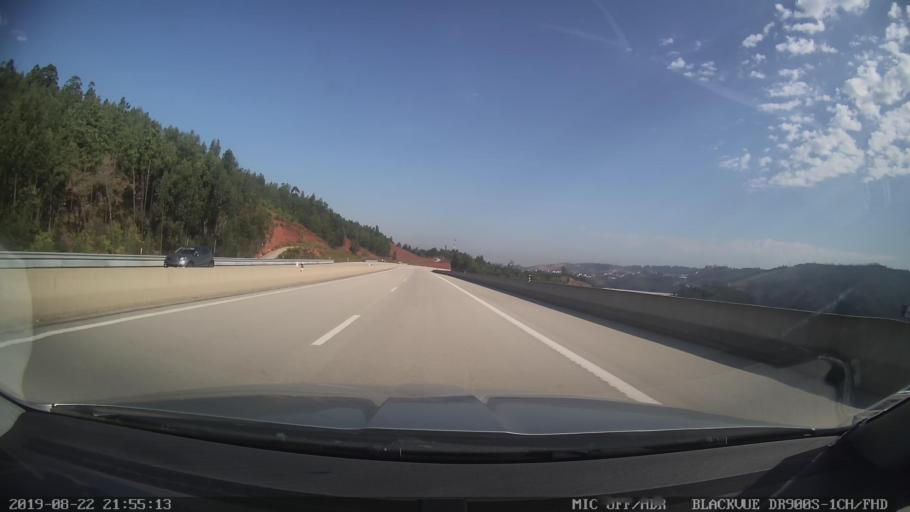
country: PT
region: Coimbra
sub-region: Coimbra
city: Coimbra
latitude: 40.1497
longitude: -8.3838
